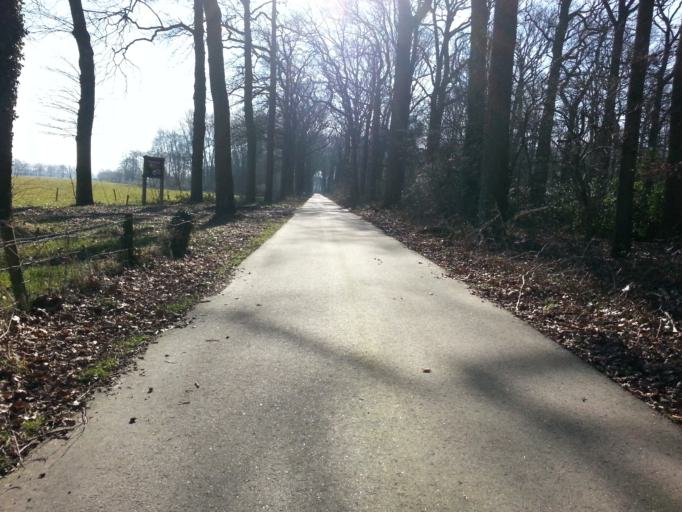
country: NL
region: Utrecht
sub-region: Gemeente Woudenberg
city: Woudenberg
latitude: 52.0658
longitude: 5.4391
